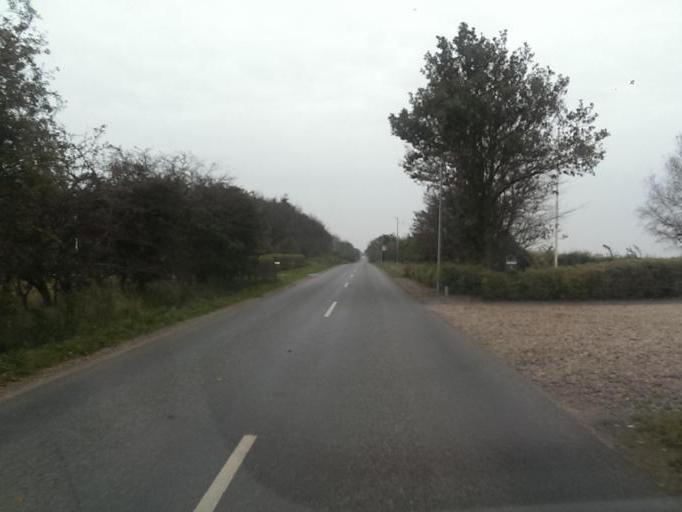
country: DK
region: South Denmark
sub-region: Esbjerg Kommune
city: Tjaereborg
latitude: 55.4838
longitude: 8.5551
